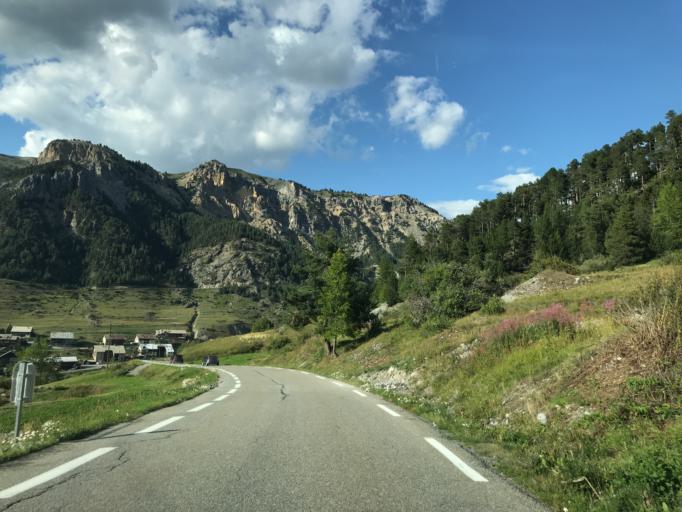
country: IT
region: Piedmont
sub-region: Provincia di Torino
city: Claviere
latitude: 44.8646
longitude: 6.7245
